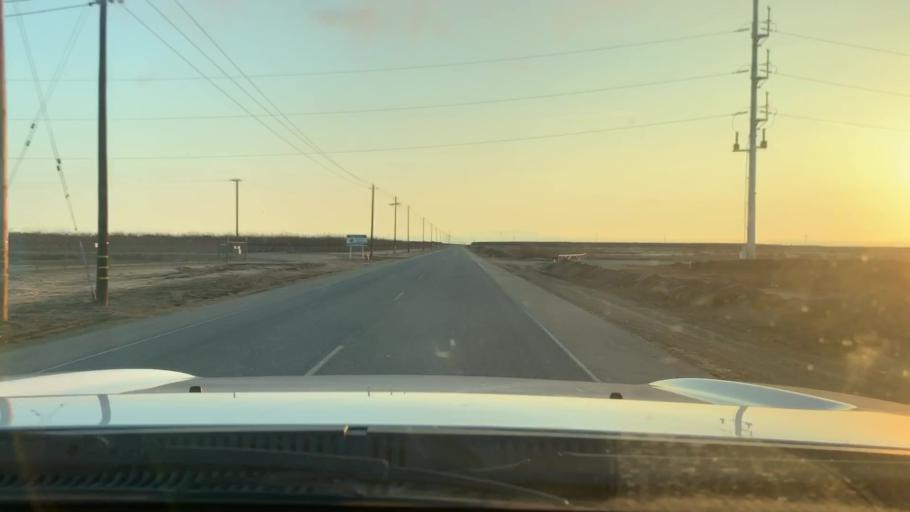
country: US
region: California
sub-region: Kern County
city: Buttonwillow
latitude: 35.5005
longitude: -119.4491
